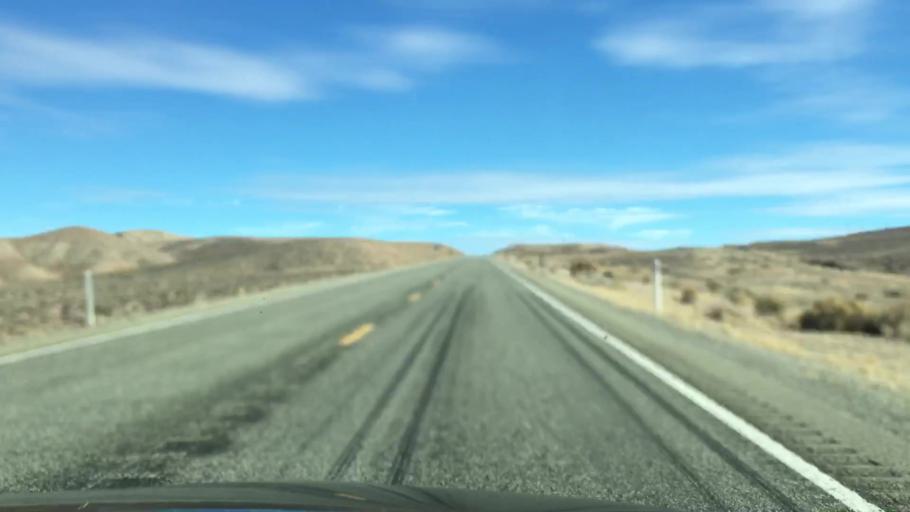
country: US
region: Nevada
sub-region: Lyon County
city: Yerington
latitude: 39.0460
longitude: -118.9671
